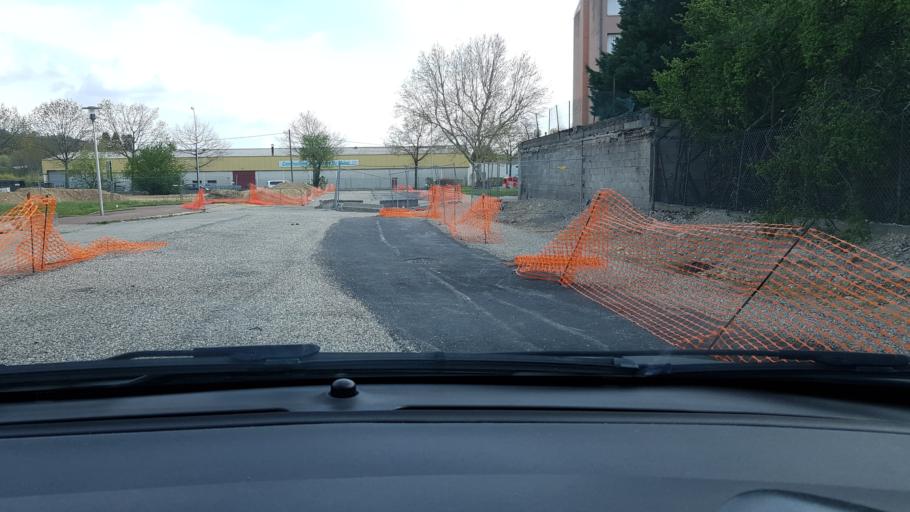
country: FR
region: Rhone-Alpes
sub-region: Departement du Rhone
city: Brignais
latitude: 45.6686
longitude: 4.7596
